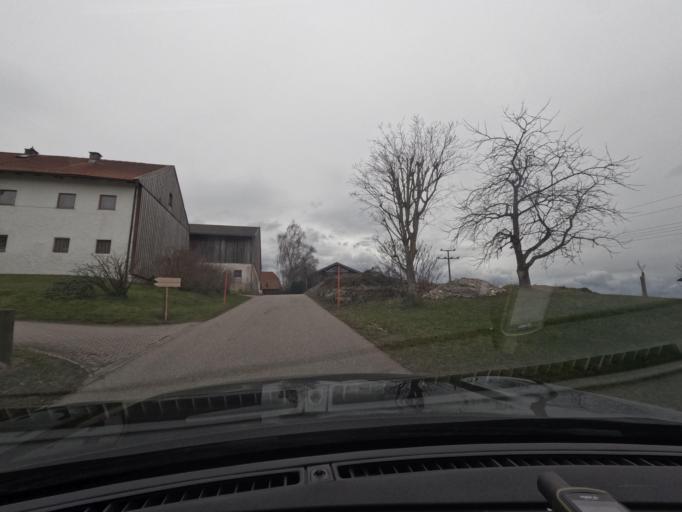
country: DE
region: Bavaria
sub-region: Upper Bavaria
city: Surberg
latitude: 47.8698
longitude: 12.6865
